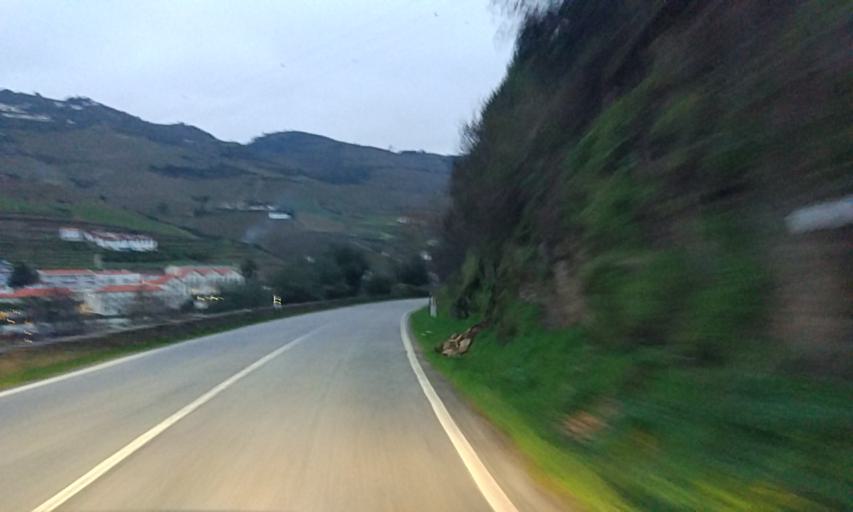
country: PT
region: Vila Real
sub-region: Sabrosa
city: Vilela
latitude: 41.1863
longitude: -7.5462
